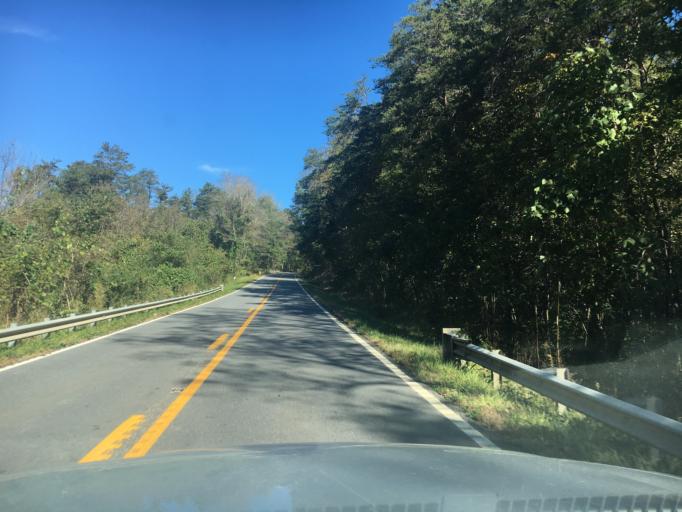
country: US
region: North Carolina
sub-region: Rutherford County
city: Spindale
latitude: 35.4714
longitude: -81.8837
